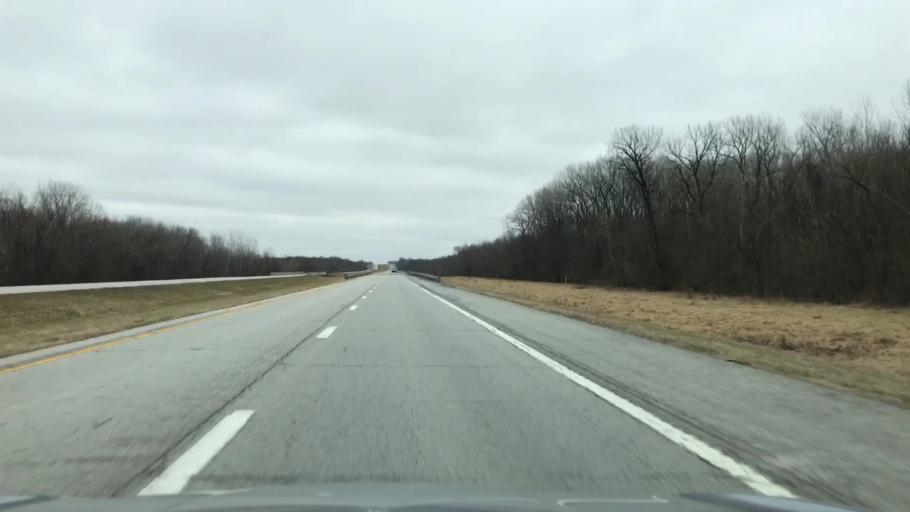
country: US
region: Missouri
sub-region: Linn County
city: Linneus
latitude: 39.7779
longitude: -93.2267
